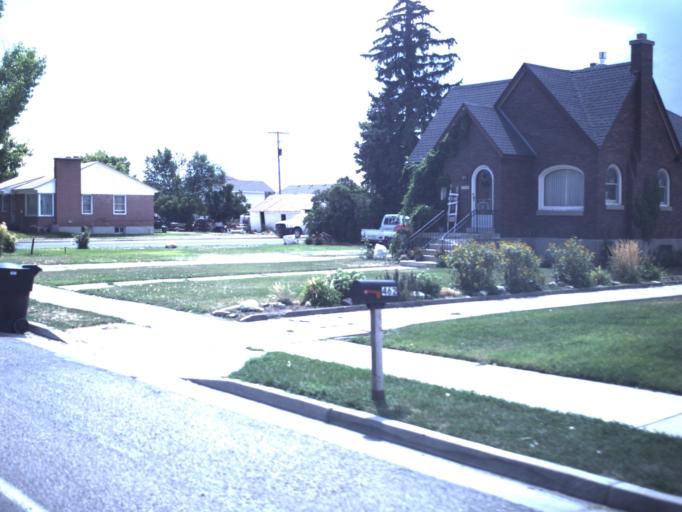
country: US
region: Utah
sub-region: Box Elder County
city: Garland
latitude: 41.7363
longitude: -112.1625
